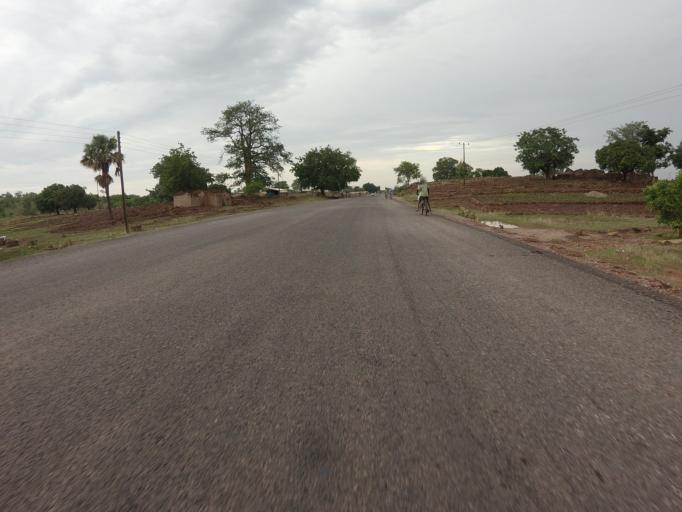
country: GH
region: Upper East
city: Bolgatanga
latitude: 10.8488
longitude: -0.6797
